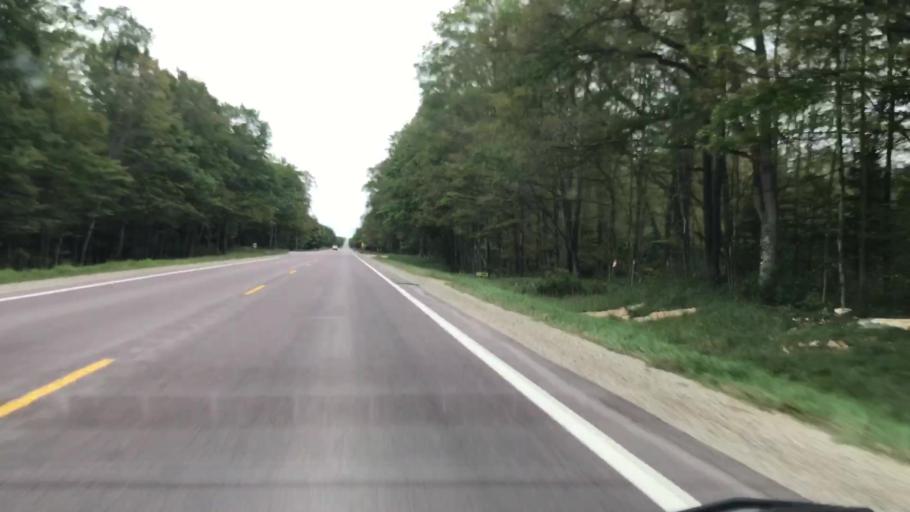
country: US
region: Michigan
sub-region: Luce County
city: Newberry
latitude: 46.2482
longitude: -85.5724
